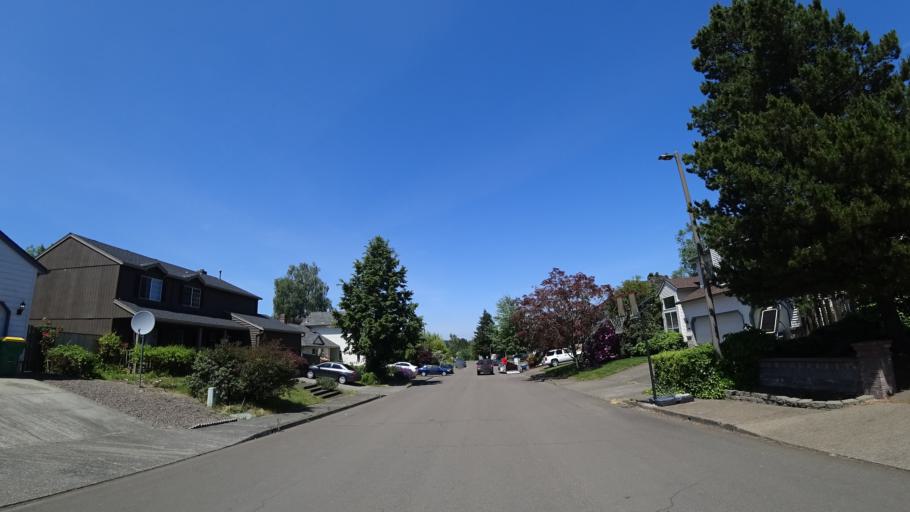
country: US
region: Oregon
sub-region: Washington County
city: King City
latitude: 45.4291
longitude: -122.8142
